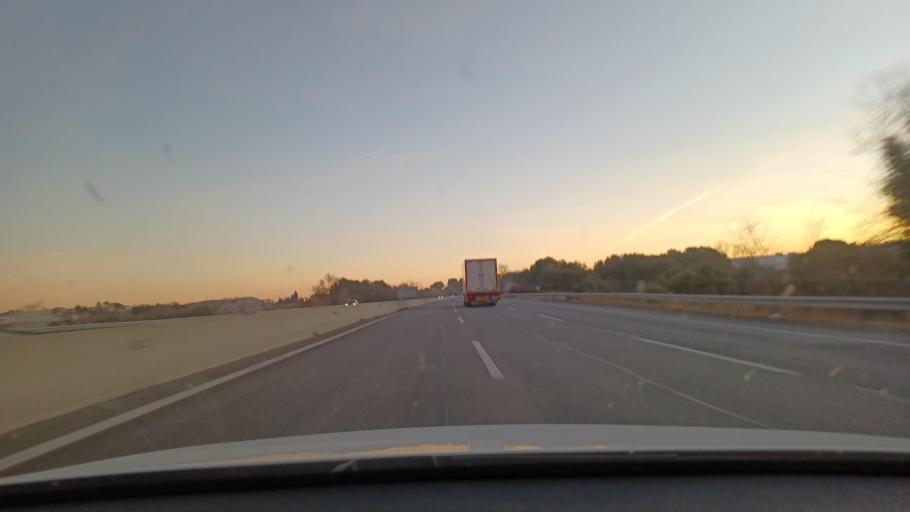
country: ES
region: Catalonia
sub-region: Provincia de Barcelona
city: Vilobi del Penedes
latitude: 41.3244
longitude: 1.6451
